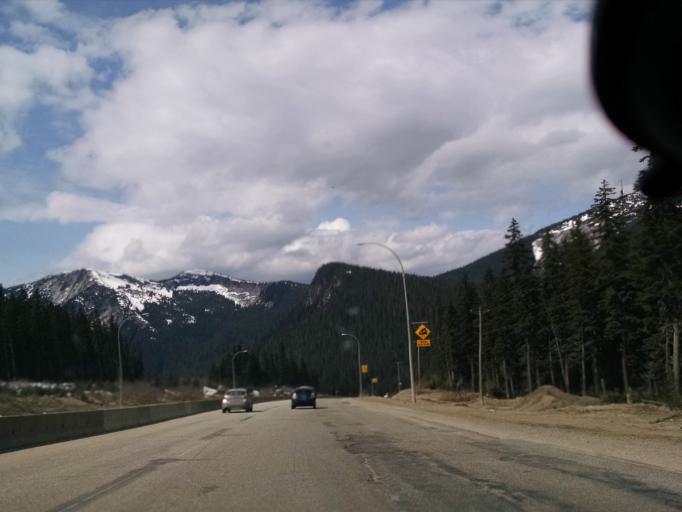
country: CA
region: British Columbia
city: Hope
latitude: 49.5958
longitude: -121.1258
